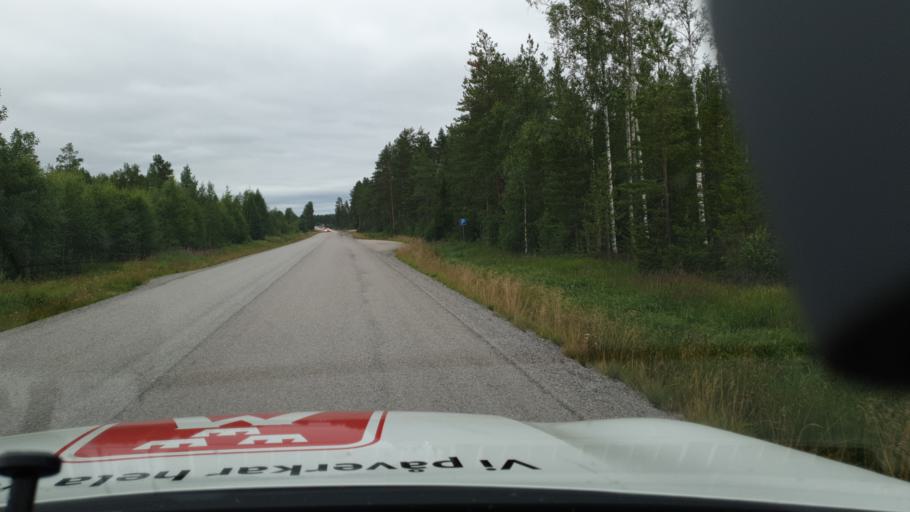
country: SE
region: Vaesterbotten
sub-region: Umea Kommun
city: Ersmark
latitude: 63.9050
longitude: 20.3136
